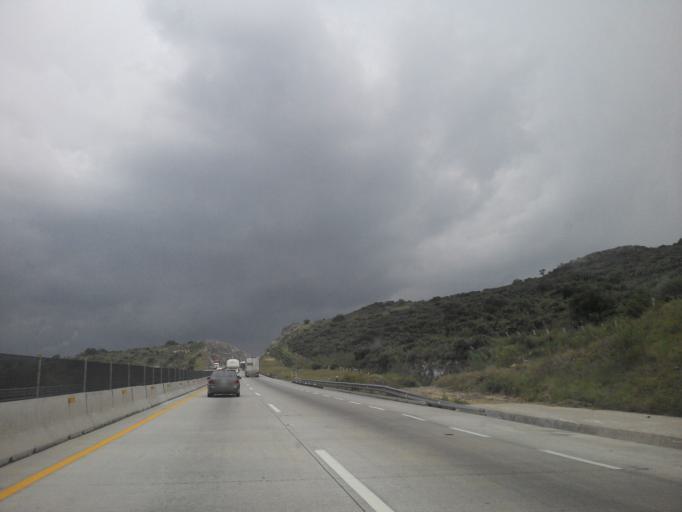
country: MX
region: Hidalgo
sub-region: San Agustin Tlaxiaca
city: Oriental de Zapata
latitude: 19.9653
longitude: -99.0078
